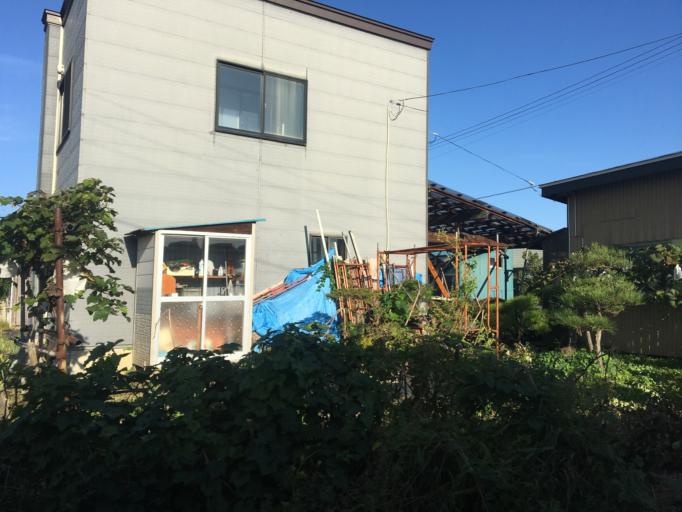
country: JP
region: Aomori
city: Kuroishi
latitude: 40.6503
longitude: 140.5770
